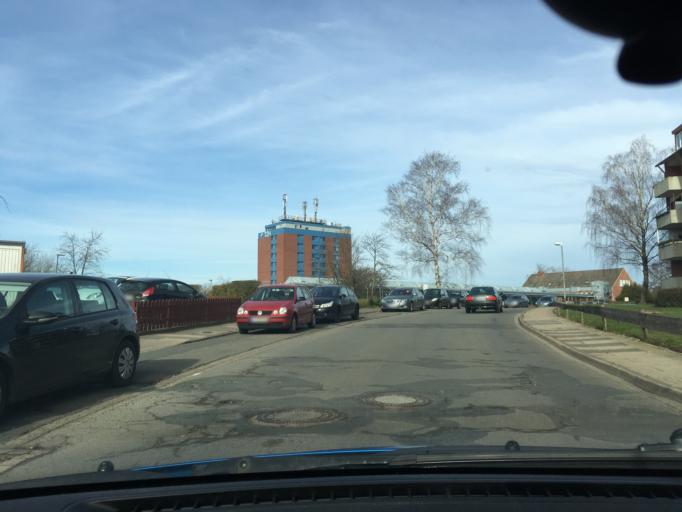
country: DE
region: Lower Saxony
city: Lueneburg
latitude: 53.2465
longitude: 10.4275
